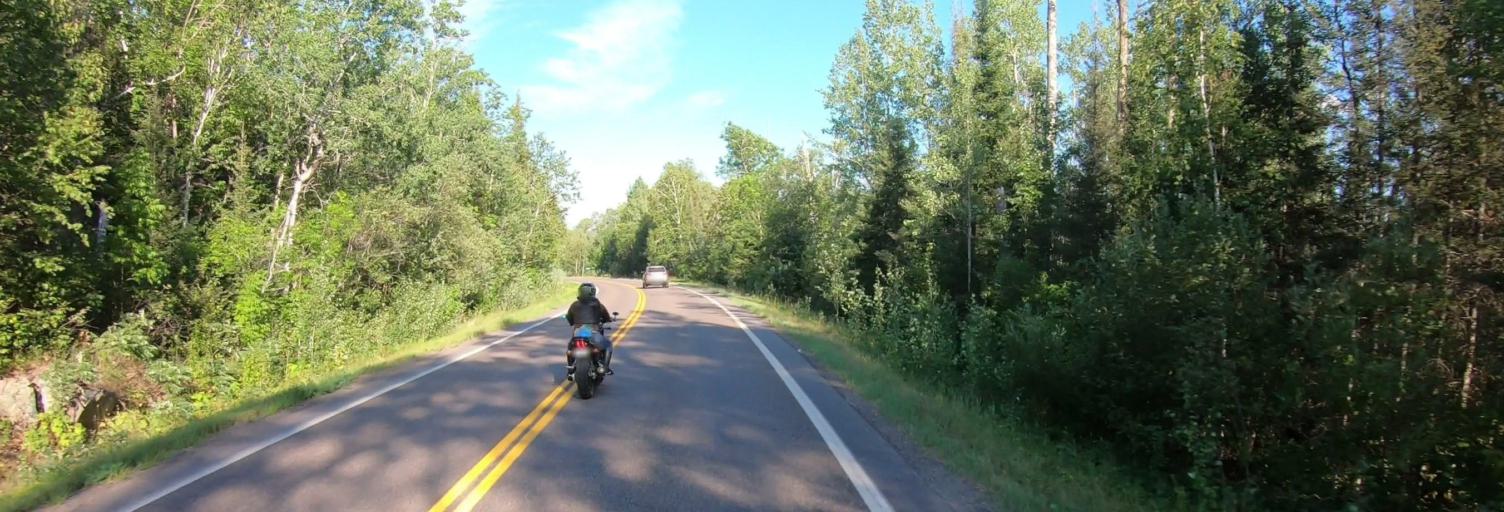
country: US
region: Minnesota
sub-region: Saint Louis County
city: Ely
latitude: 47.9315
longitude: -91.7117
